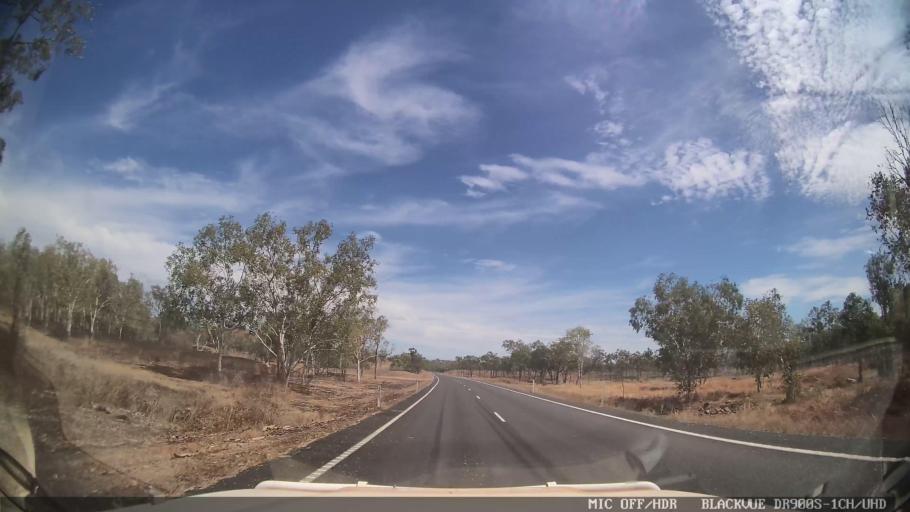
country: AU
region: Queensland
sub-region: Cook
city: Cooktown
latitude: -15.7580
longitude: 145.0008
